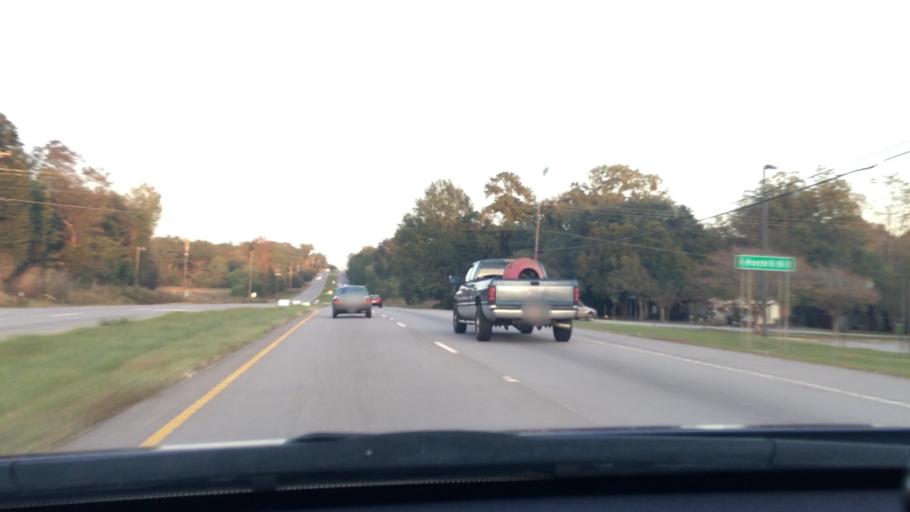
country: US
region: South Carolina
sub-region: Richland County
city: Hopkins
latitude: 33.9503
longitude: -80.8534
